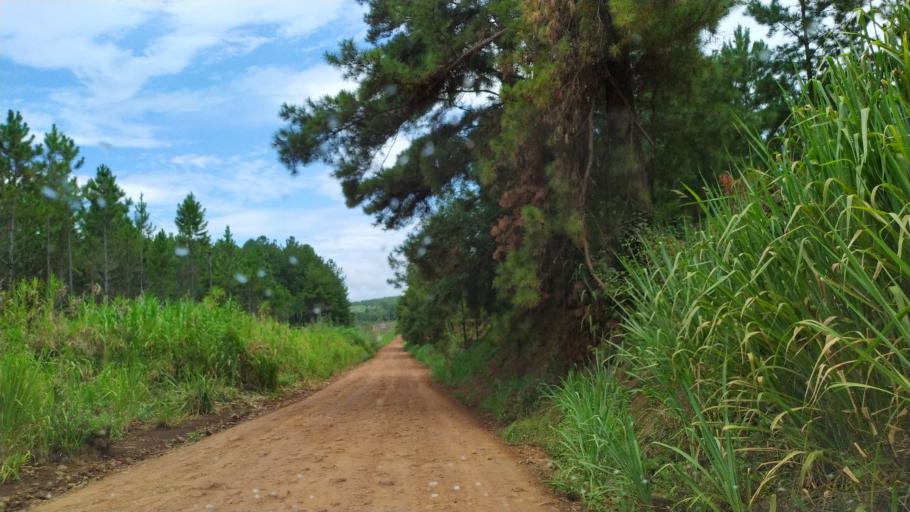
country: AR
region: Misiones
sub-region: Departamento de Eldorado
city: Eldorado
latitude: -26.4374
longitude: -54.6043
